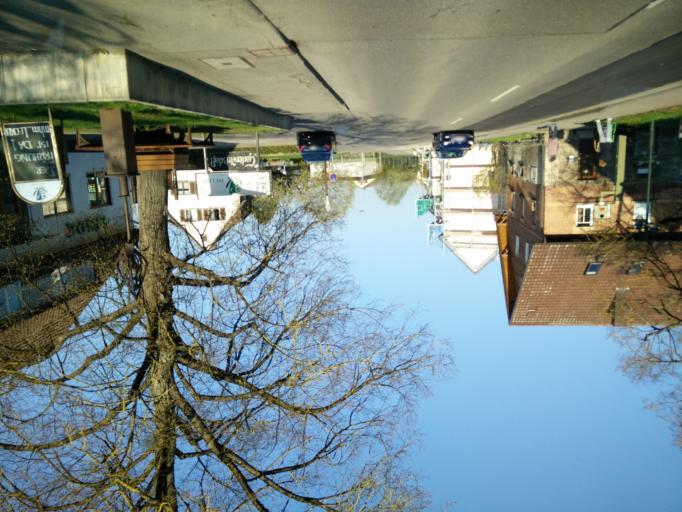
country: DE
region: Baden-Wuerttemberg
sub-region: Regierungsbezirk Stuttgart
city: Herrenberg
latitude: 48.6076
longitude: 8.8571
